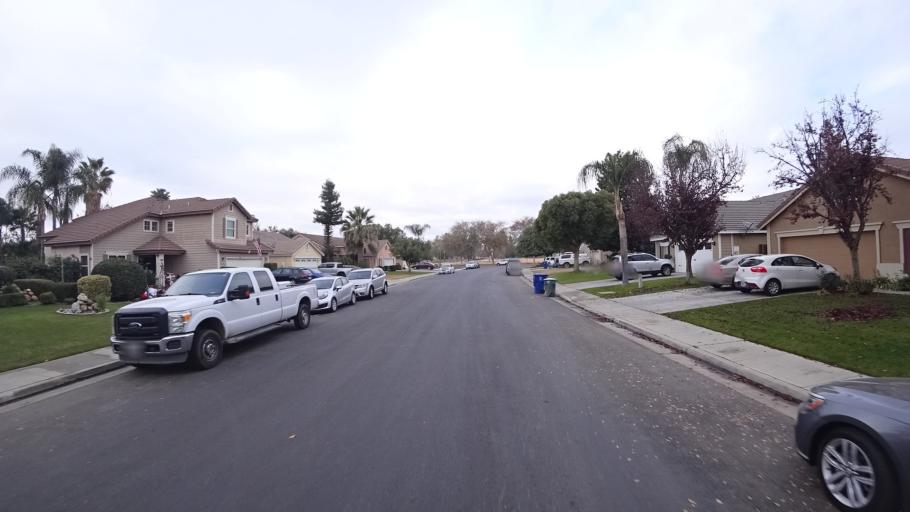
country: US
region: California
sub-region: Kern County
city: Greenacres
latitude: 35.3009
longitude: -119.0879
